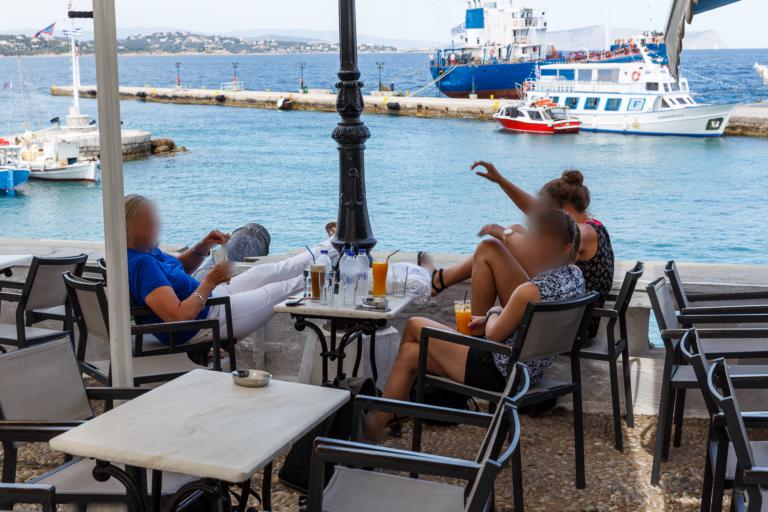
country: GR
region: Attica
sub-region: Nomos Piraios
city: Spetses
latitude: 37.2677
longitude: 23.1554
